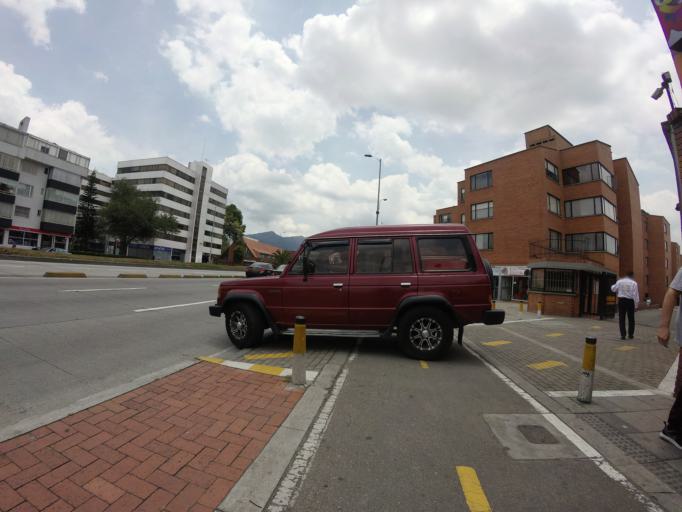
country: CO
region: Bogota D.C.
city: Barrio San Luis
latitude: 4.6944
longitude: -74.0680
